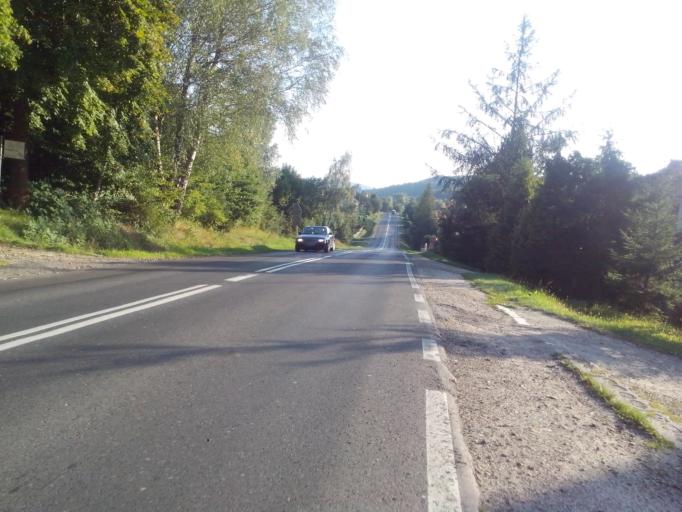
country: PL
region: Subcarpathian Voivodeship
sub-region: Powiat strzyzowski
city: Strzyzow
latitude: 49.8930
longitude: 21.8297
